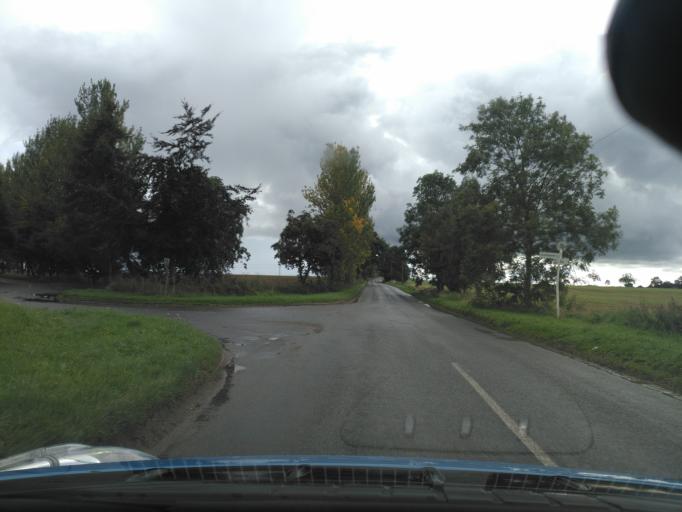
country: GB
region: England
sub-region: Oxfordshire
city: Wheatley
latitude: 51.7364
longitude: -1.1432
